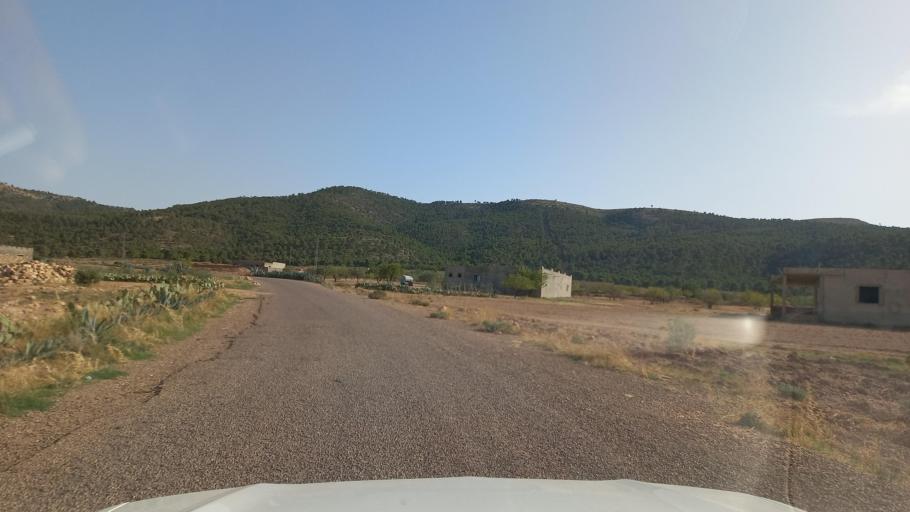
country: TN
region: Al Qasrayn
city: Kasserine
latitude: 35.3401
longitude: 8.8346
